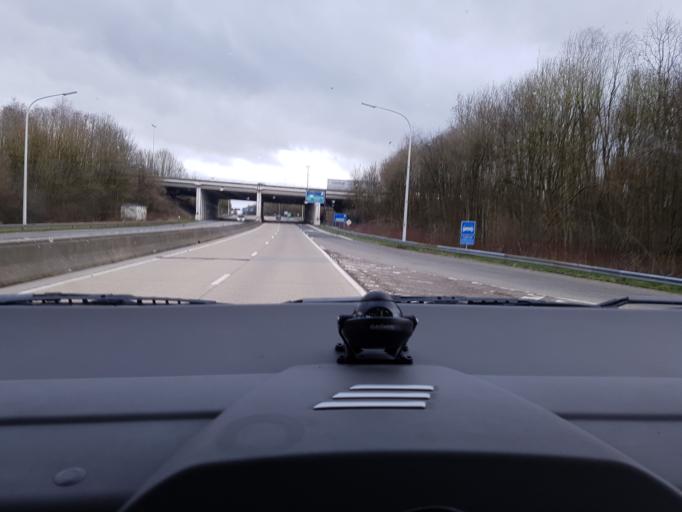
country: BE
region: Wallonia
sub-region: Province de Namur
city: Ciney
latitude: 50.2686
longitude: 5.0372
